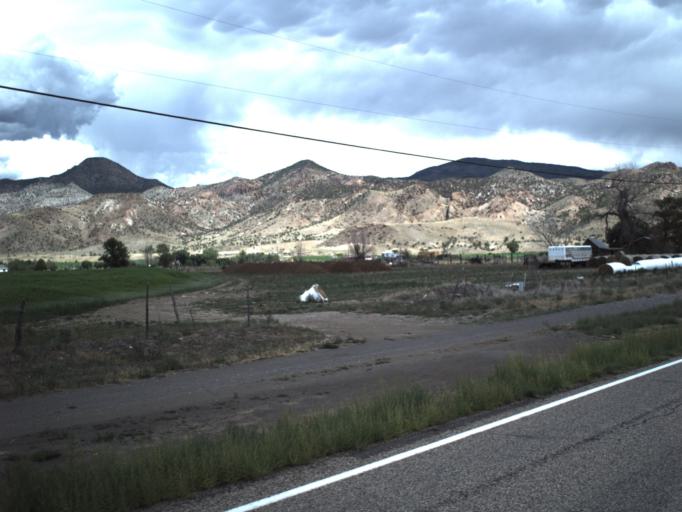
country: US
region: Utah
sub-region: Piute County
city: Junction
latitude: 38.2083
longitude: -112.1919
